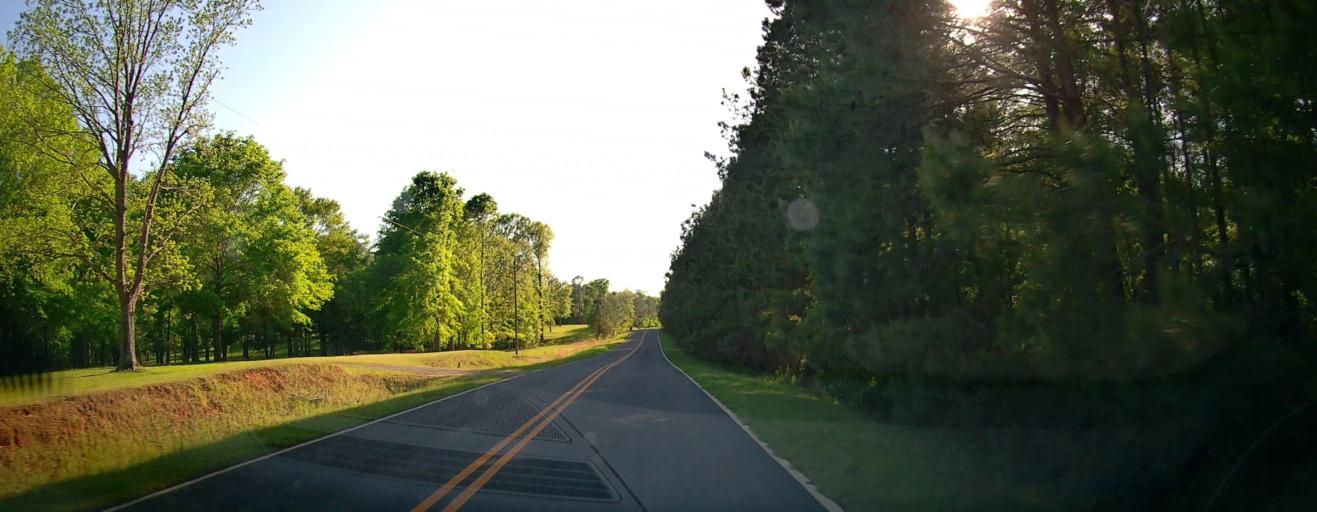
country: US
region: Georgia
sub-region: Macon County
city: Marshallville
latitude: 32.3873
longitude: -83.8532
